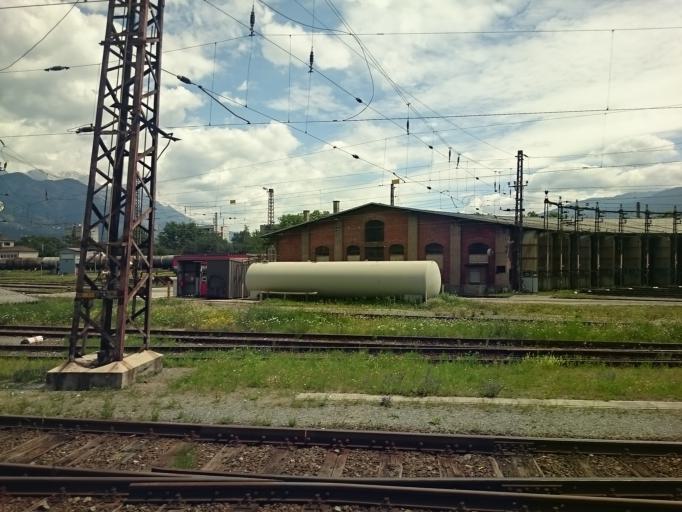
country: AT
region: Tyrol
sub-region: Innsbruck Stadt
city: Innsbruck
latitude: 47.2582
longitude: 11.4011
